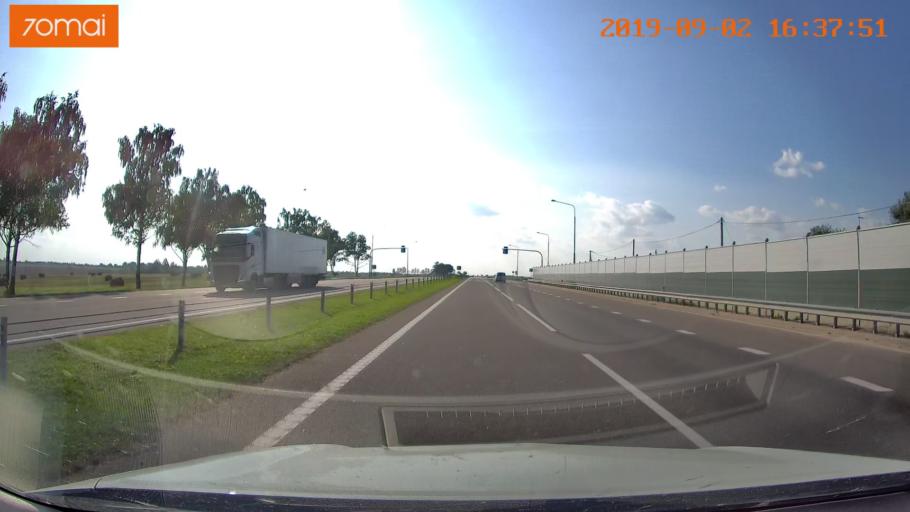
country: BY
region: Minsk
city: Smilavichy
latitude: 53.7614
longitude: 27.9334
